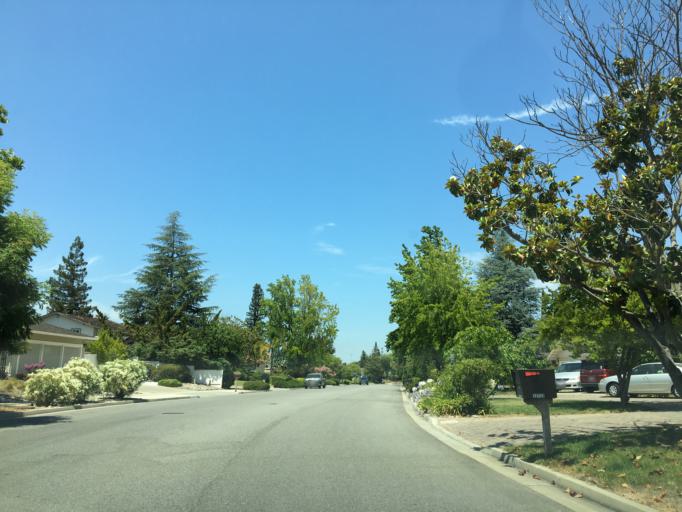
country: US
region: California
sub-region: Santa Clara County
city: Saratoga
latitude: 37.2840
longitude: -122.0123
